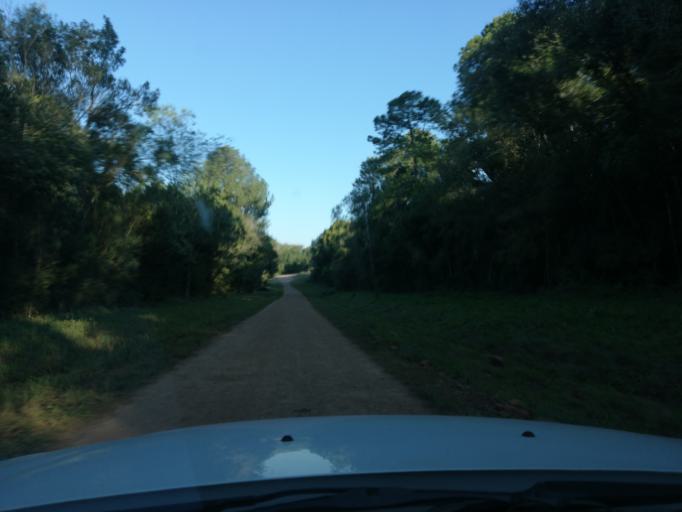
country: AR
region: Misiones
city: Cerro Cora
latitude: -27.6219
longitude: -55.7053
